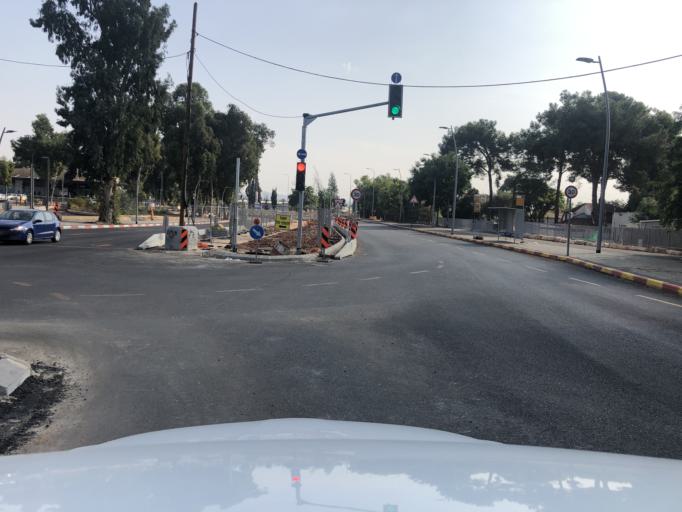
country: IL
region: Central District
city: Kfar Saba
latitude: 32.1705
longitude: 34.9262
